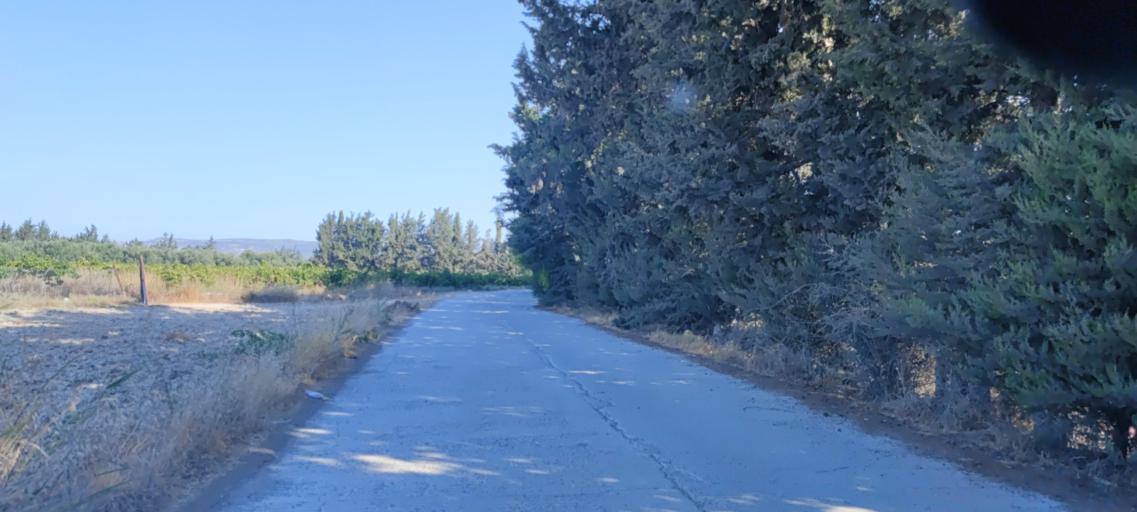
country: CY
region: Limassol
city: Sotira
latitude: 34.6683
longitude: 32.7978
